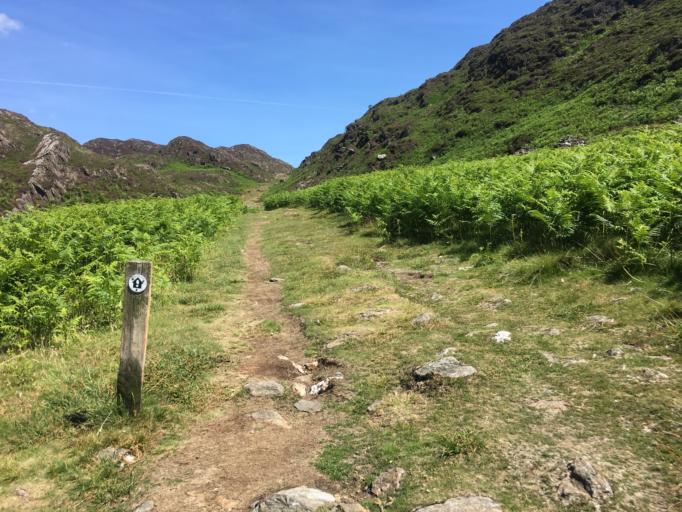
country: GB
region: Wales
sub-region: Gwynedd
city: Penrhyndeudraeth
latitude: 53.0076
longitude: -4.0816
